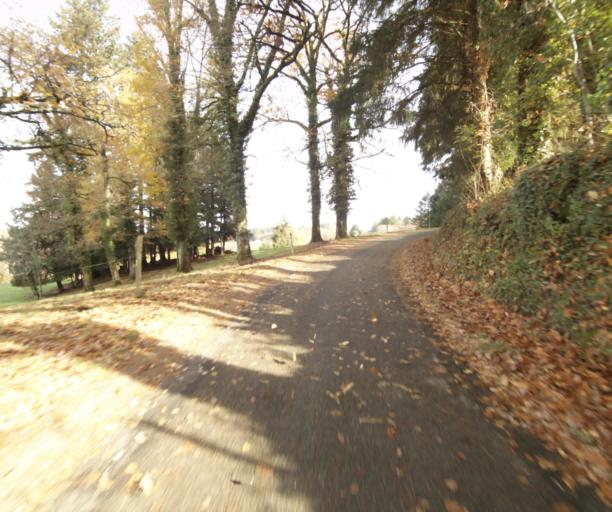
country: FR
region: Limousin
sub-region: Departement de la Correze
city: Sainte-Fortunade
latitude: 45.1946
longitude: 1.7396
